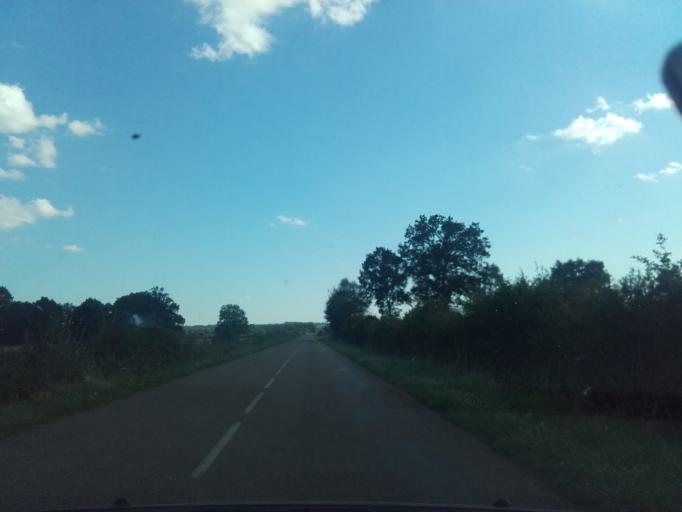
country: FR
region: Bourgogne
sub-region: Departement de Saone-et-Loire
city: Epinac
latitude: 47.0029
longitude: 4.4763
